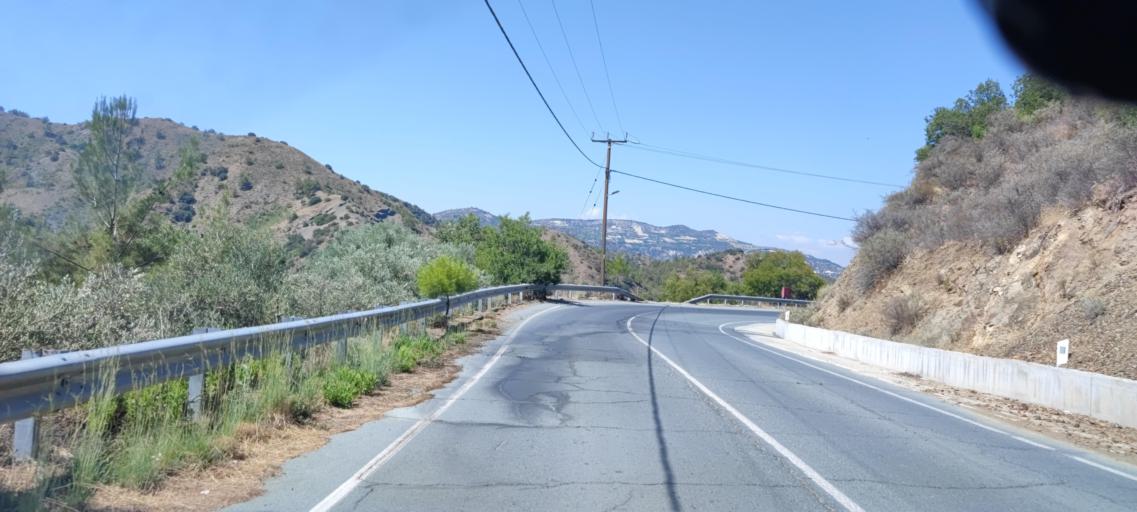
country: CY
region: Lefkosia
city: Kakopetria
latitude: 34.8966
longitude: 32.8259
